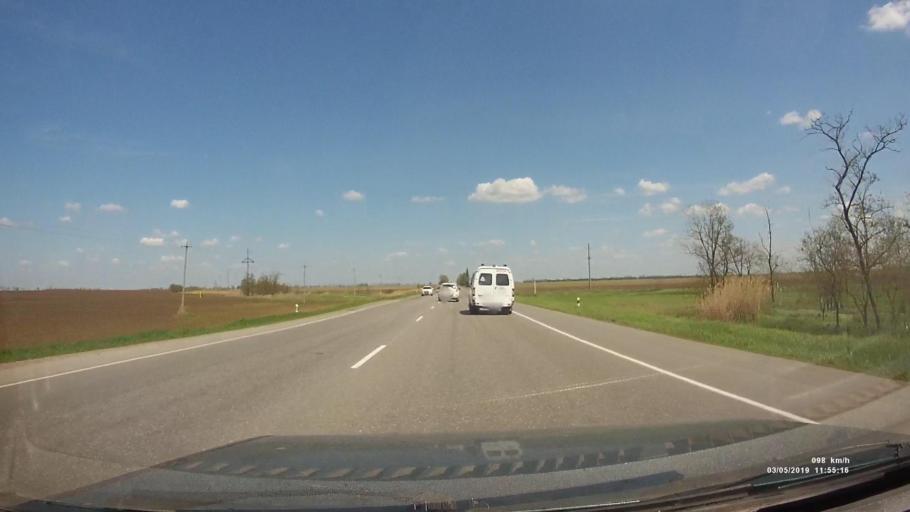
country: RU
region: Rostov
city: Bagayevskaya
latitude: 47.1789
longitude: 40.2896
